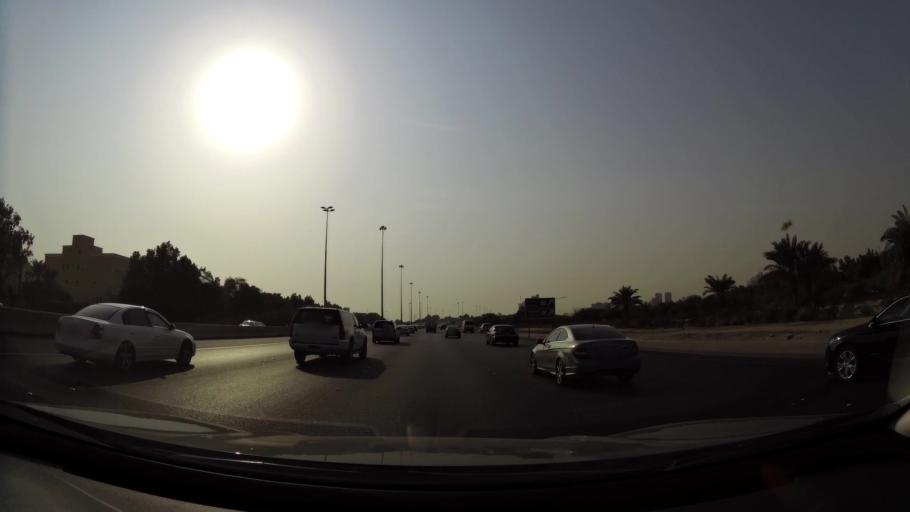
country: KW
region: Muhafazat Hawalli
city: Salwa
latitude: 29.2758
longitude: 48.0810
